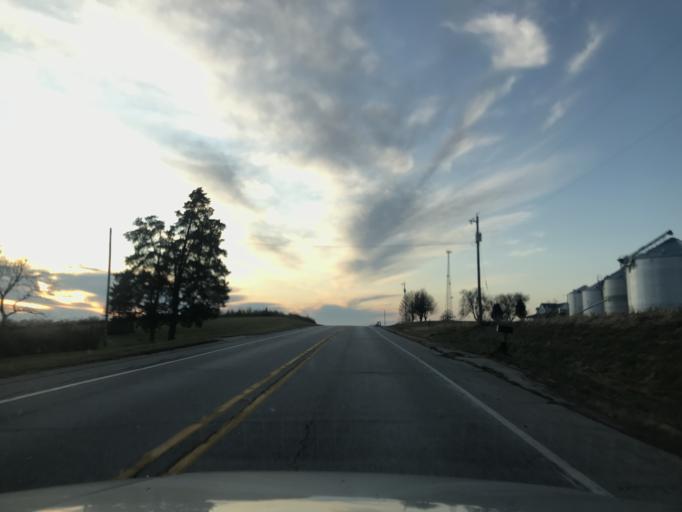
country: US
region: Illinois
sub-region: Henderson County
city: Oquawka
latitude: 41.0187
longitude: -90.8427
